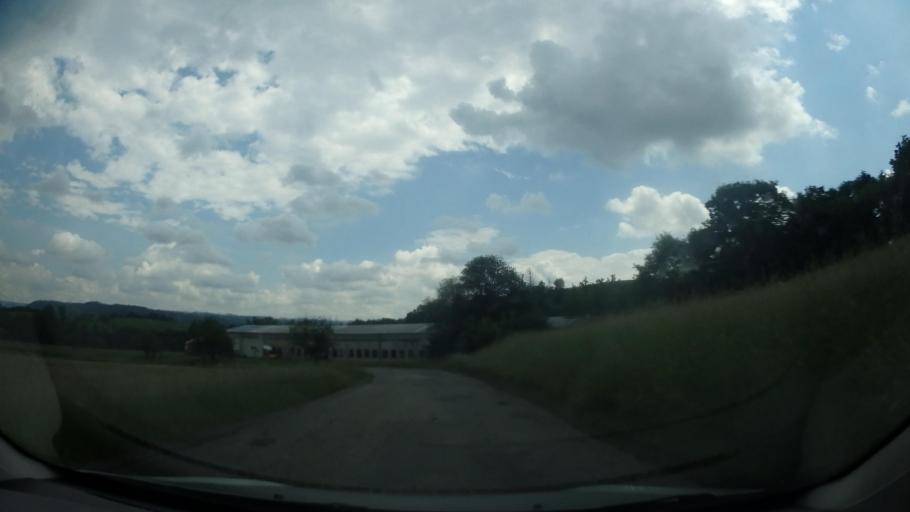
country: CZ
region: South Moravian
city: Doubravice nad Svitavou
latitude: 49.4604
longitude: 16.6031
